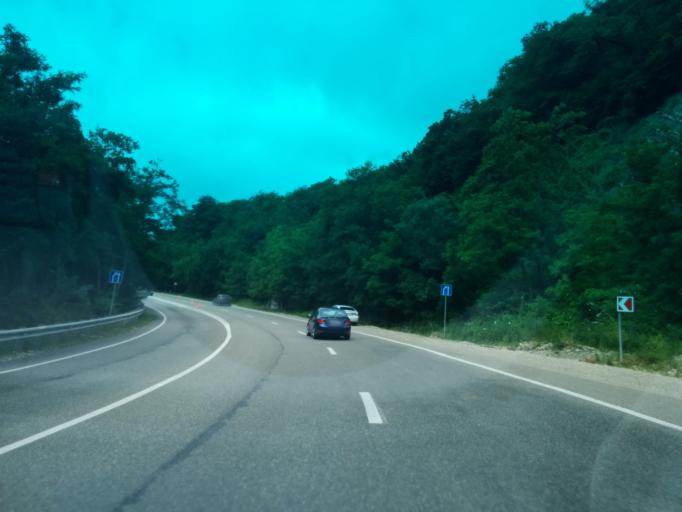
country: RU
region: Krasnodarskiy
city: Nebug
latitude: 44.1775
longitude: 38.9598
